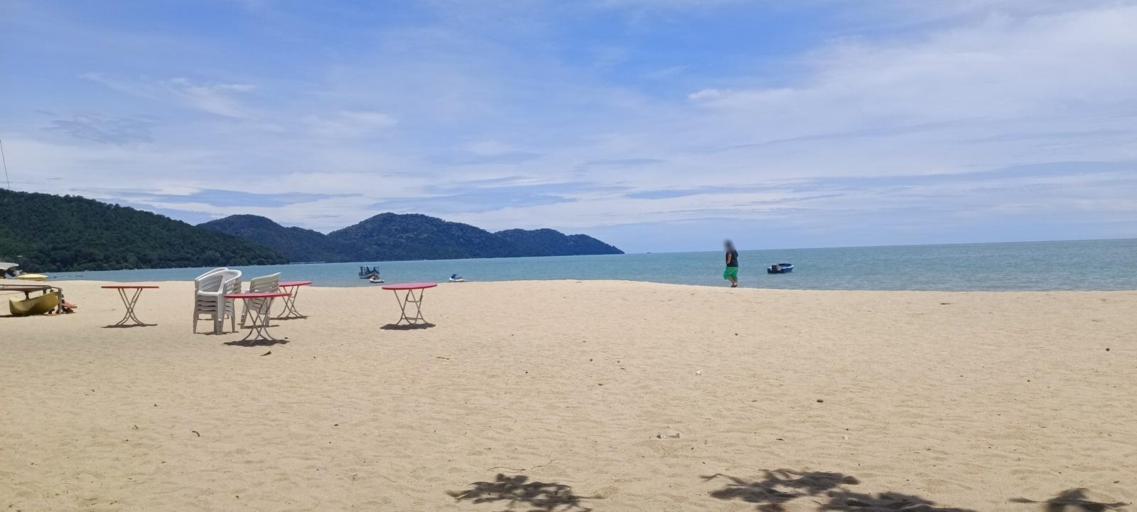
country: MY
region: Penang
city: Tanjung Tokong
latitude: 5.4716
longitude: 100.2443
